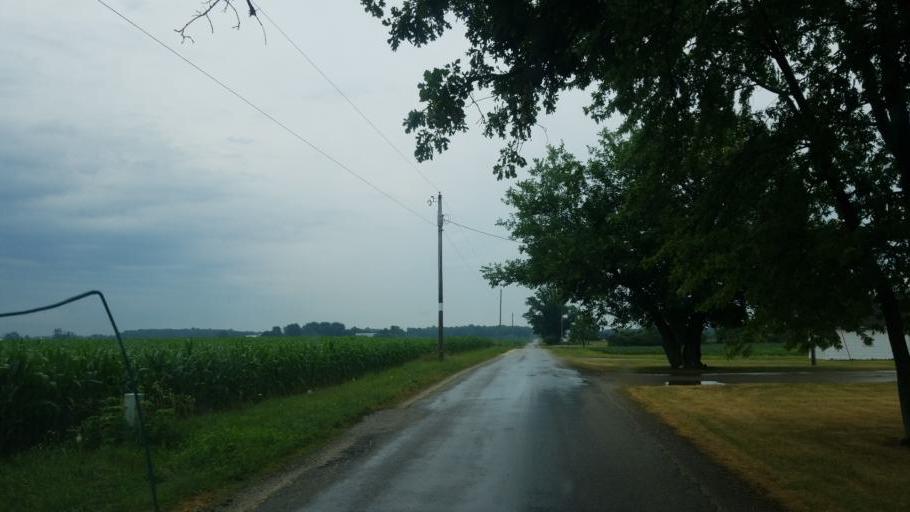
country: US
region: Ohio
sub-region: Williams County
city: Edgerton
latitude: 41.4195
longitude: -84.6703
